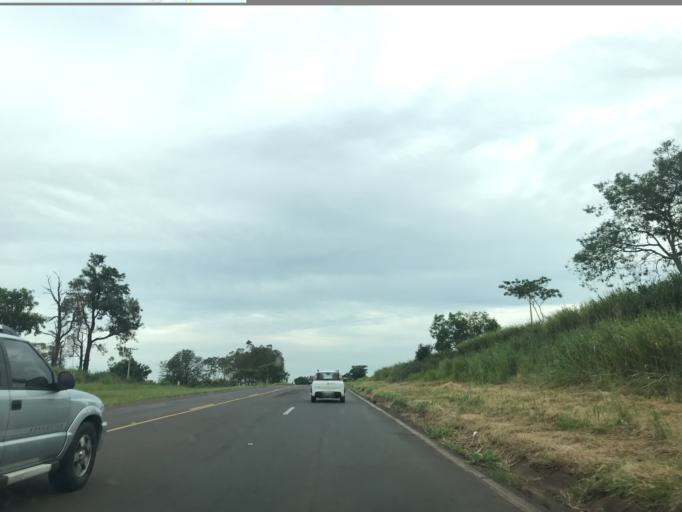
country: BR
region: Sao Paulo
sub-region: Tupa
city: Tupa
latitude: -21.6066
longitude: -50.4723
